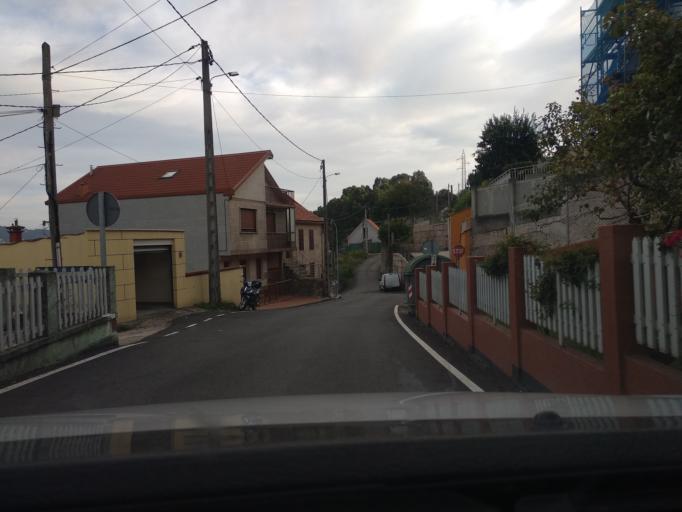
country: ES
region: Galicia
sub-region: Provincia de Pontevedra
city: Moana
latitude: 42.2921
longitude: -8.7386
